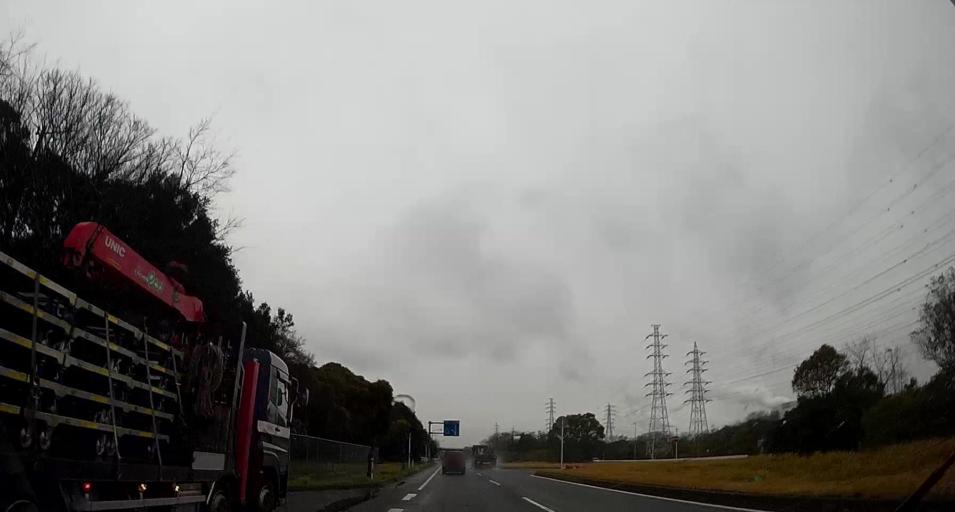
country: JP
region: Chiba
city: Ichihara
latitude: 35.4627
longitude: 140.0169
